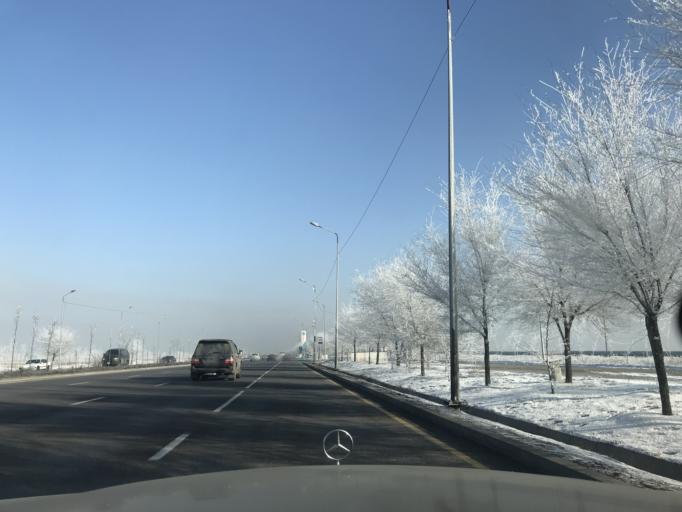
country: KZ
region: Almaty Oblysy
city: Burunday
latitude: 43.2934
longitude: 76.8309
